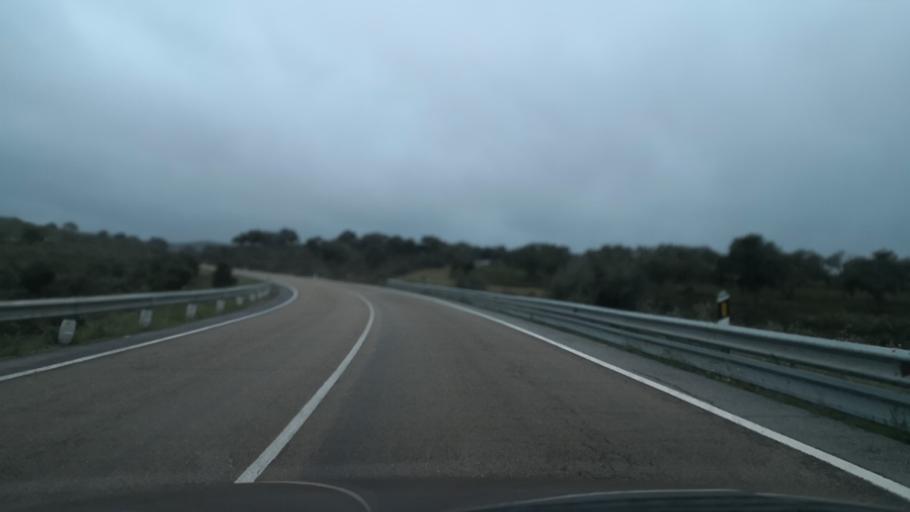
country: ES
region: Extremadura
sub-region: Provincia de Caceres
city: Malpartida de Caceres
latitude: 39.3057
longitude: -6.5162
